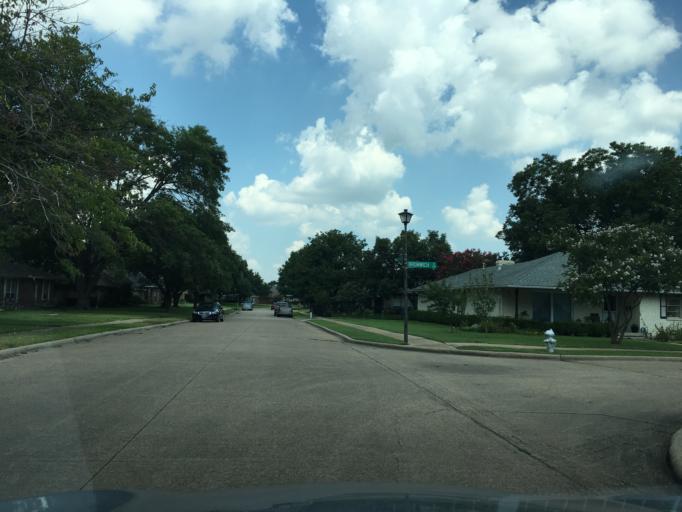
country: US
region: Texas
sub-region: Dallas County
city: Garland
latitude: 32.9386
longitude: -96.6431
